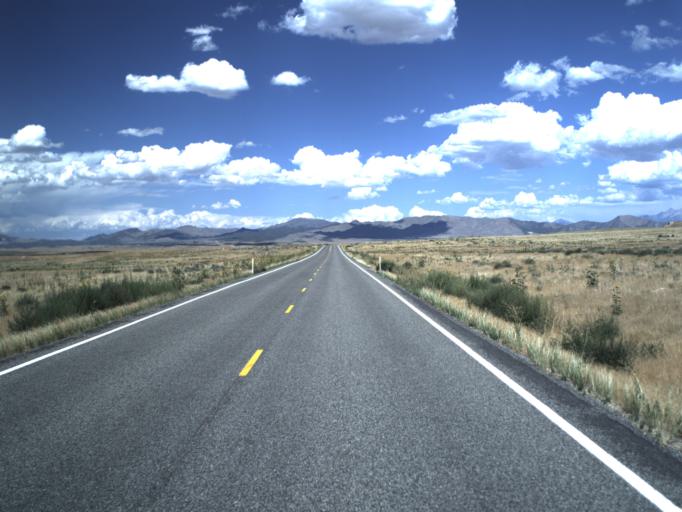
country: US
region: Utah
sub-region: Millard County
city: Delta
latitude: 39.6620
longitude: -112.2787
